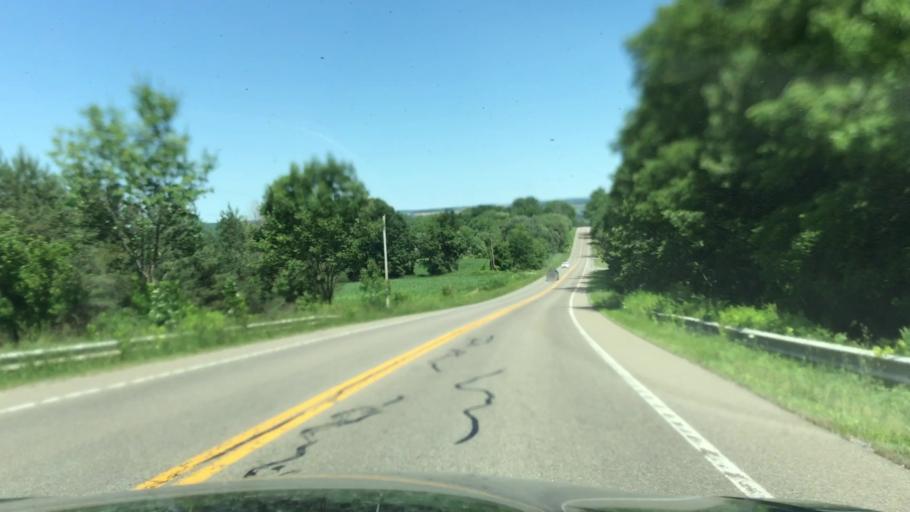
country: US
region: New York
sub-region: Livingston County
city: Mount Morris
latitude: 42.7561
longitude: -77.9013
